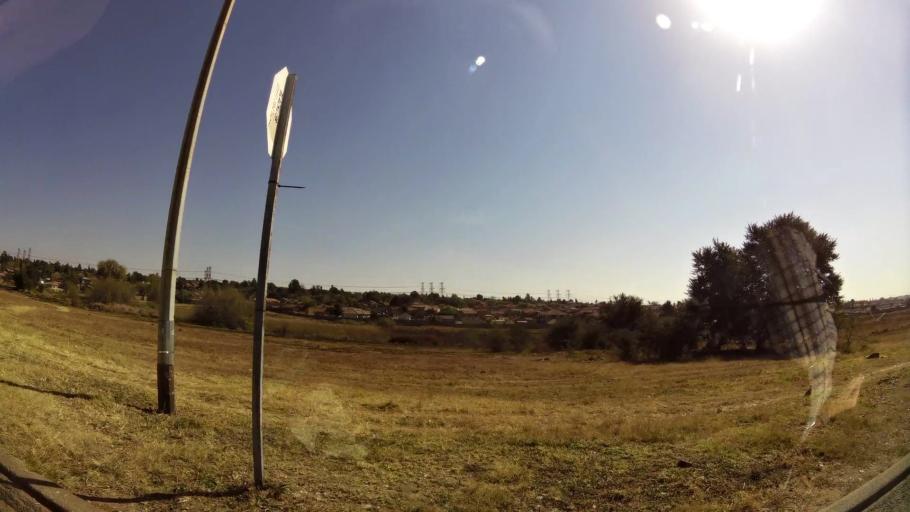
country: ZA
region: Gauteng
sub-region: Ekurhuleni Metropolitan Municipality
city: Tembisa
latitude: -26.0482
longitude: 28.2166
